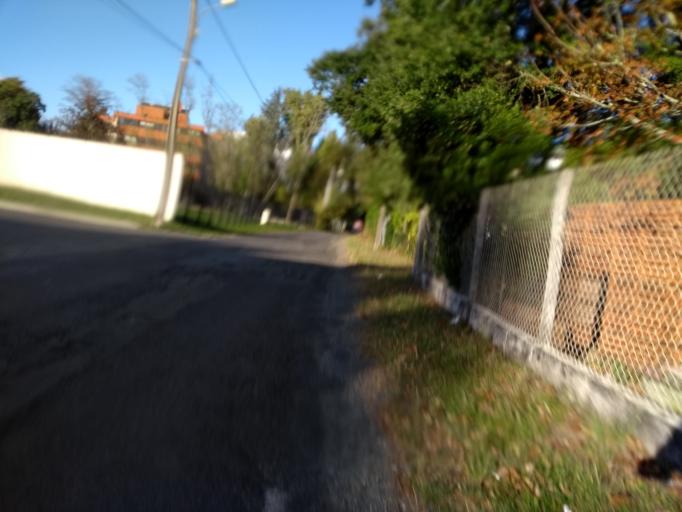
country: FR
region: Aquitaine
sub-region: Departement de la Gironde
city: Canejan
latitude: 44.7556
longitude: -0.6249
